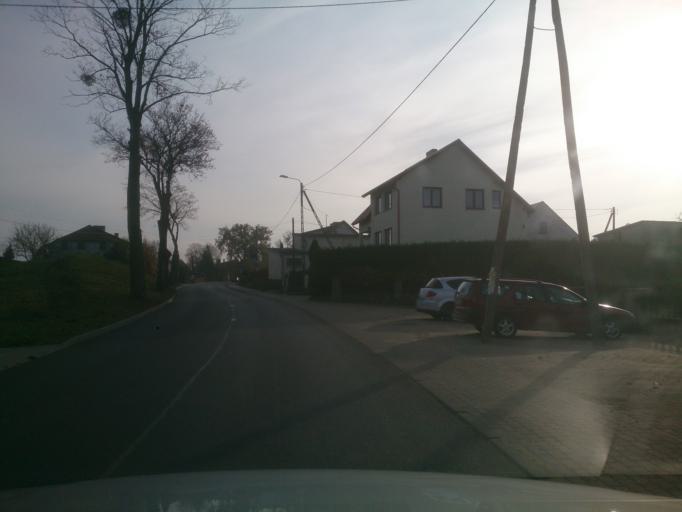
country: PL
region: Kujawsko-Pomorskie
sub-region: Powiat brodnicki
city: Brodnica
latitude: 53.3357
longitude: 19.3753
